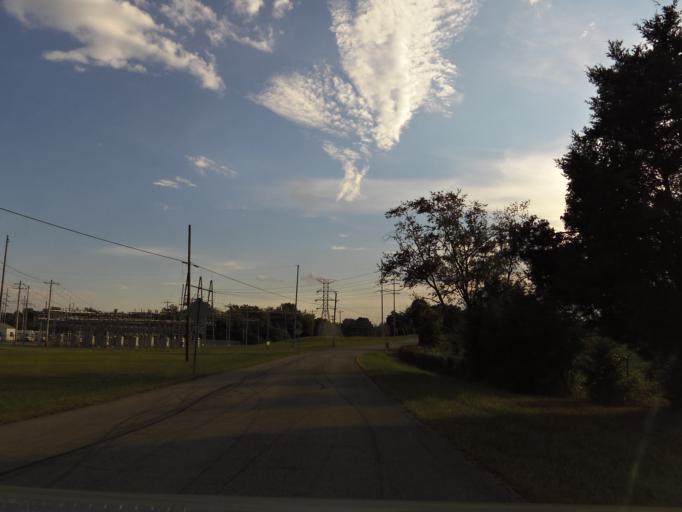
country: US
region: Tennessee
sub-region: Blount County
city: Alcoa
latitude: 35.7982
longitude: -83.9649
